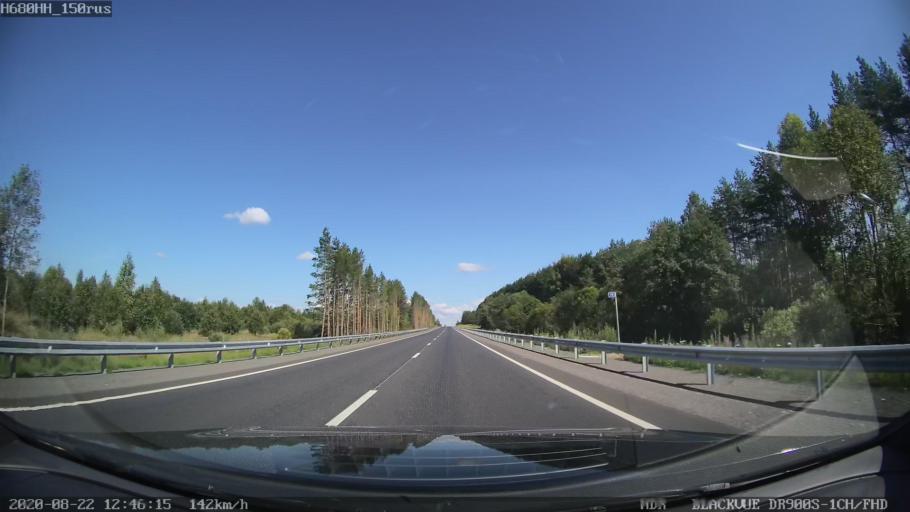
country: RU
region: Tverskaya
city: Rameshki
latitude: 57.4170
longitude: 36.1414
